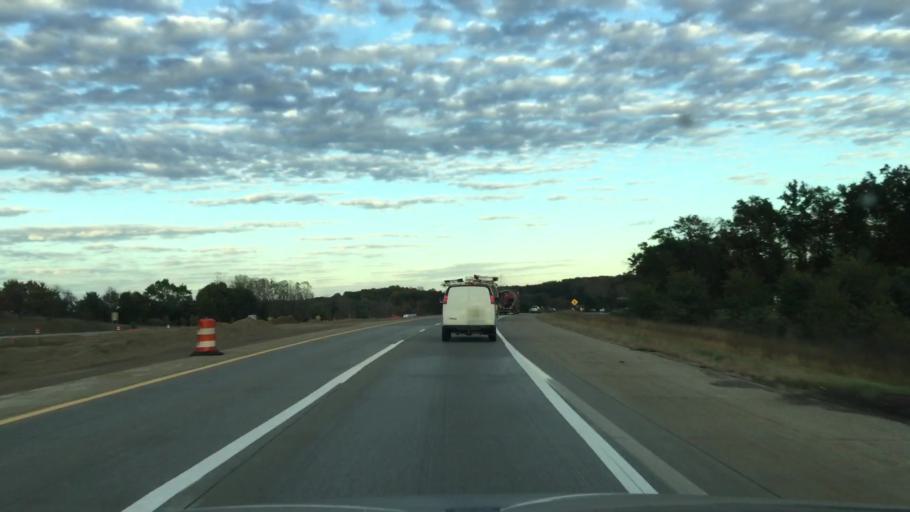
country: US
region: Michigan
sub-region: Jackson County
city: Michigan Center
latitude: 42.2802
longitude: -84.3056
